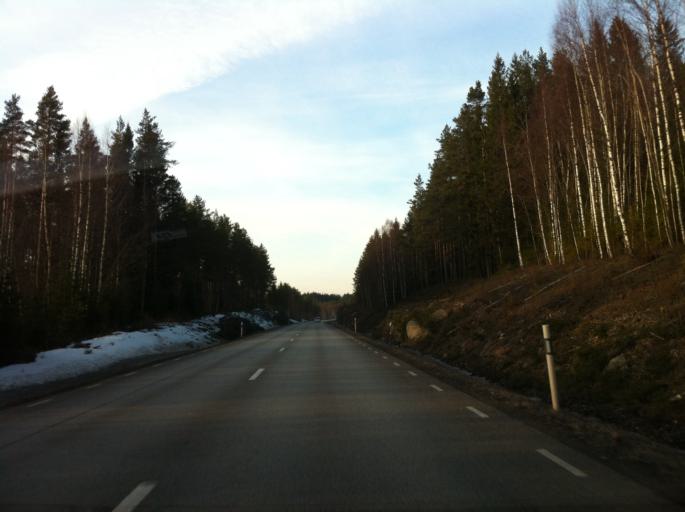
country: SE
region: Vaermland
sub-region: Filipstads Kommun
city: Lesjofors
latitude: 60.0403
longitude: 14.1476
